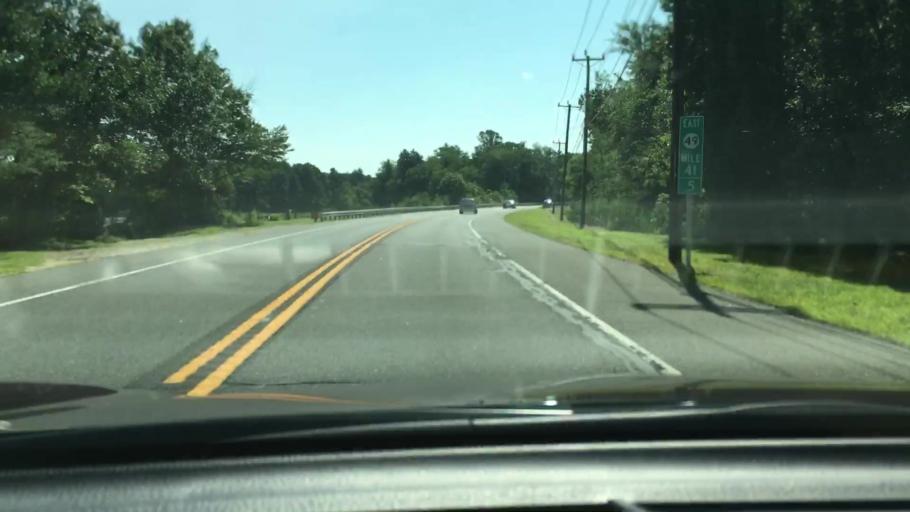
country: US
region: New Jersey
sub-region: Cumberland County
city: Laurel Lake
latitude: 39.3741
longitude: -74.9470
